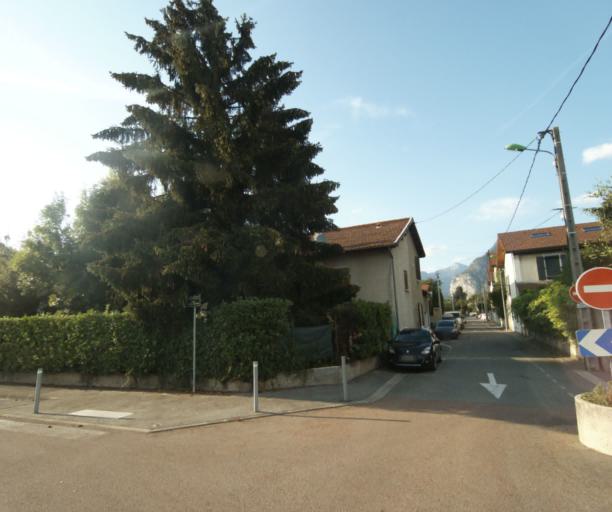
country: FR
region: Rhone-Alpes
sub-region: Departement de l'Isere
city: Seyssinet-Pariset
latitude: 45.1824
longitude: 5.6994
